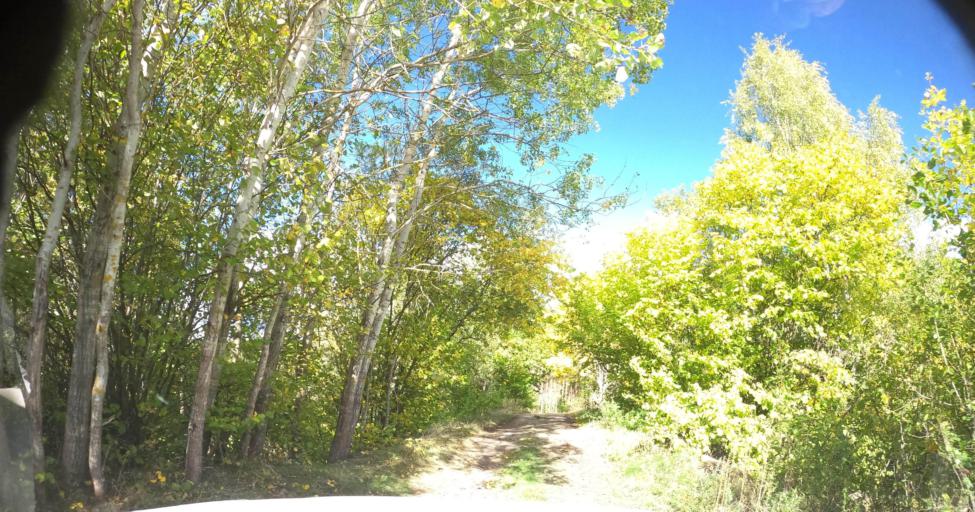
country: PL
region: West Pomeranian Voivodeship
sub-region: Powiat szczecinecki
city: Lubowo
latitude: 53.5902
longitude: 16.4371
